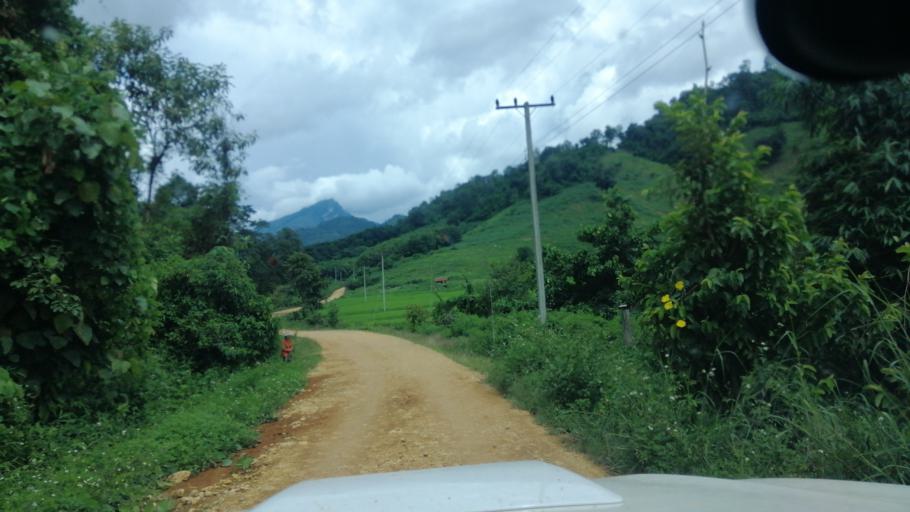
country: TH
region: Phayao
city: Phu Sang
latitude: 19.7153
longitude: 100.4881
